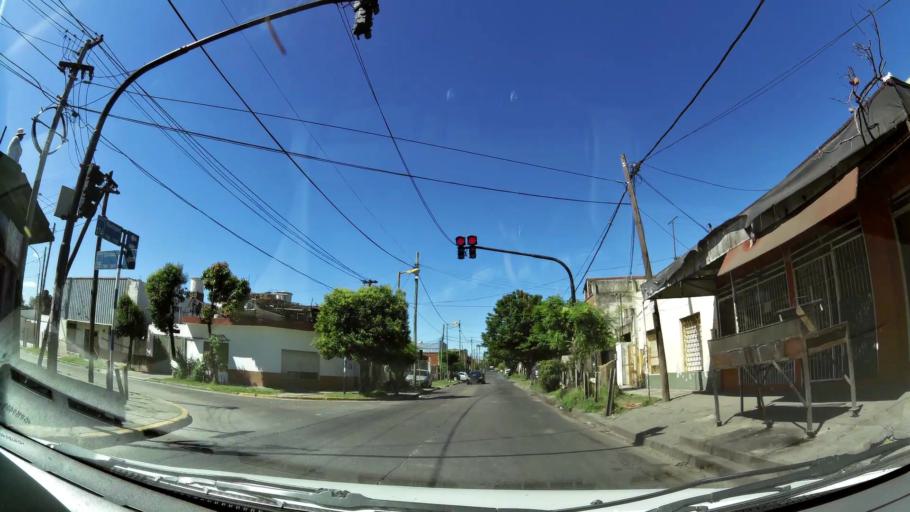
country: AR
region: Buenos Aires
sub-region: Partido de General San Martin
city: General San Martin
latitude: -34.5258
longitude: -58.5663
